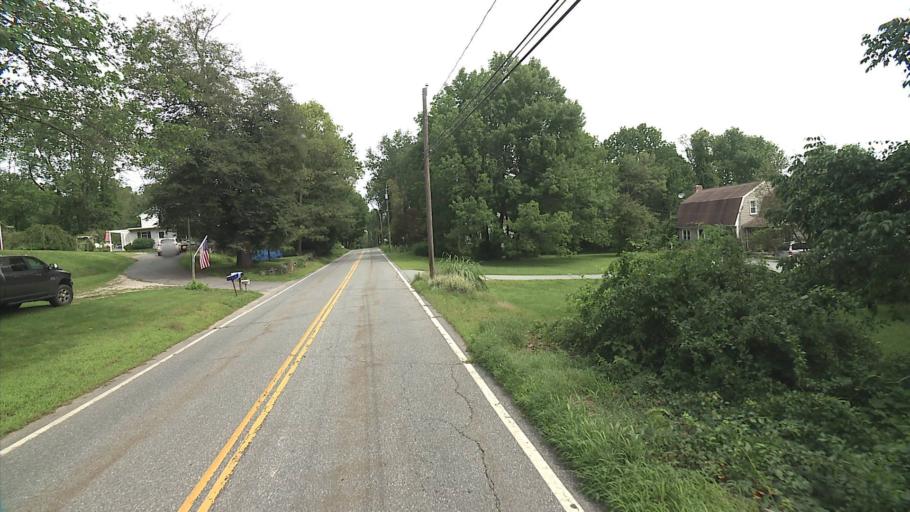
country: US
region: Massachusetts
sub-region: Worcester County
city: Webster
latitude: 42.0174
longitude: -71.8448
